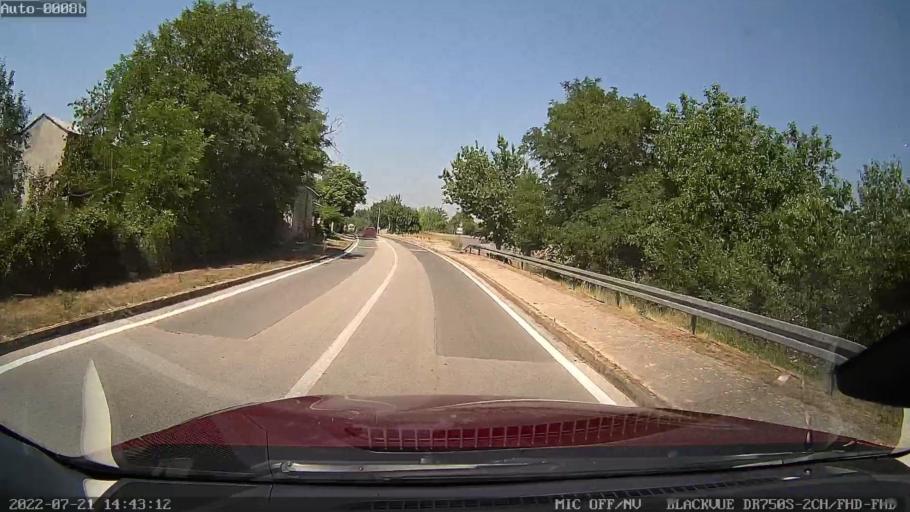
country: HR
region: Istarska
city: Pazin
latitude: 45.1055
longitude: 13.8835
